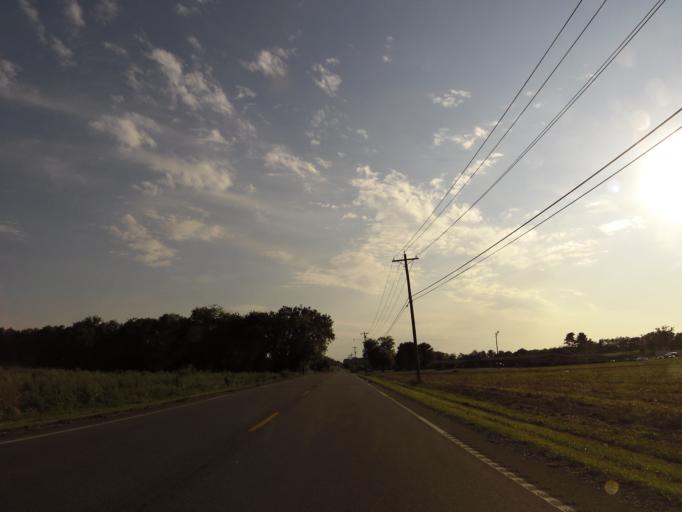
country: US
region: Tennessee
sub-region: Monroe County
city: Sweetwater
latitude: 35.5815
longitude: -84.4824
